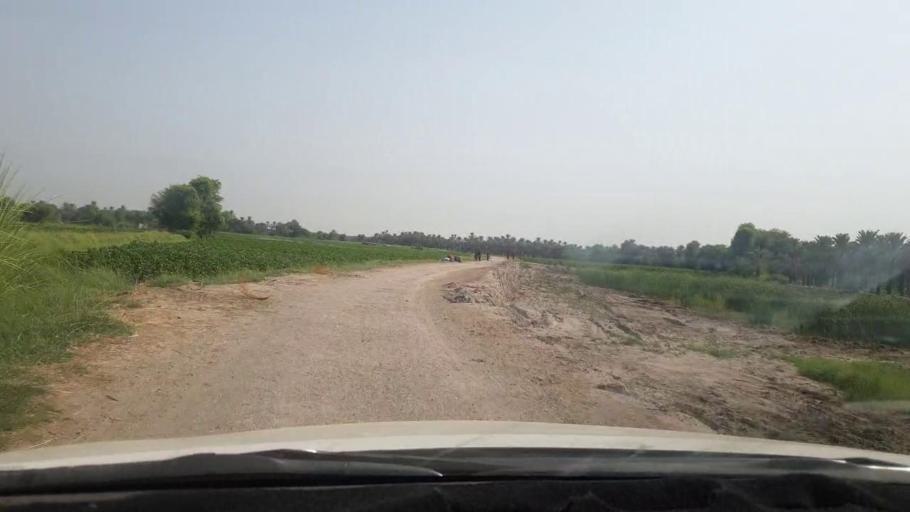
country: PK
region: Sindh
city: Rohri
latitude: 27.6079
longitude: 68.8912
